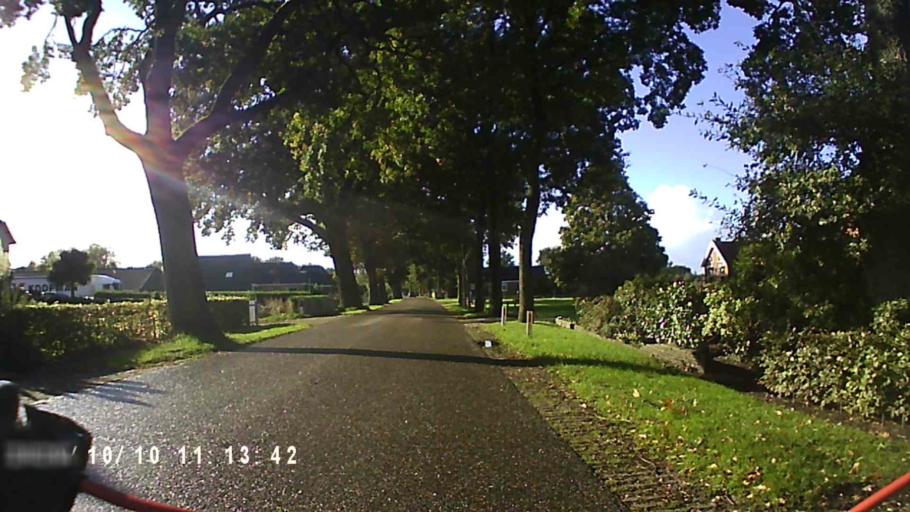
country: NL
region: Friesland
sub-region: Gemeente Smallingerland
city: Drachtstercompagnie
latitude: 53.1080
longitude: 6.2043
